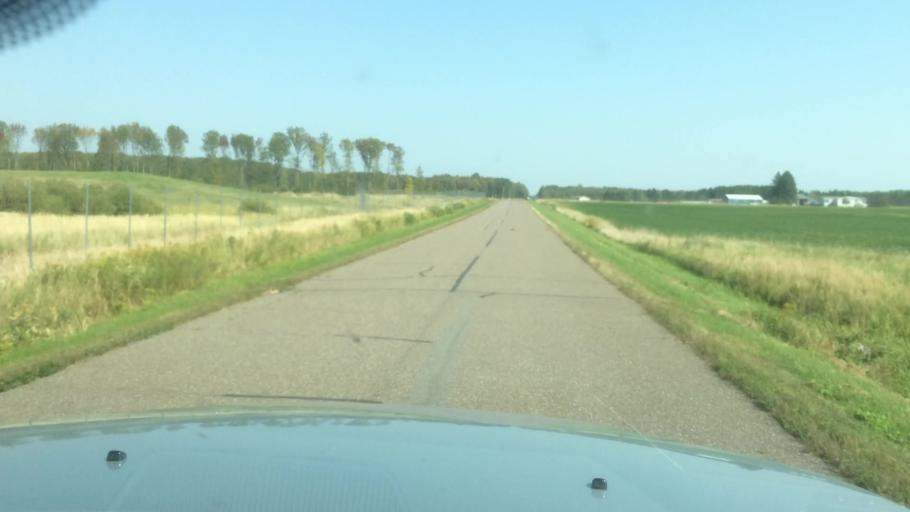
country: US
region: Wisconsin
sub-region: Taylor County
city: Medford
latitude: 45.0915
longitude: -90.3042
